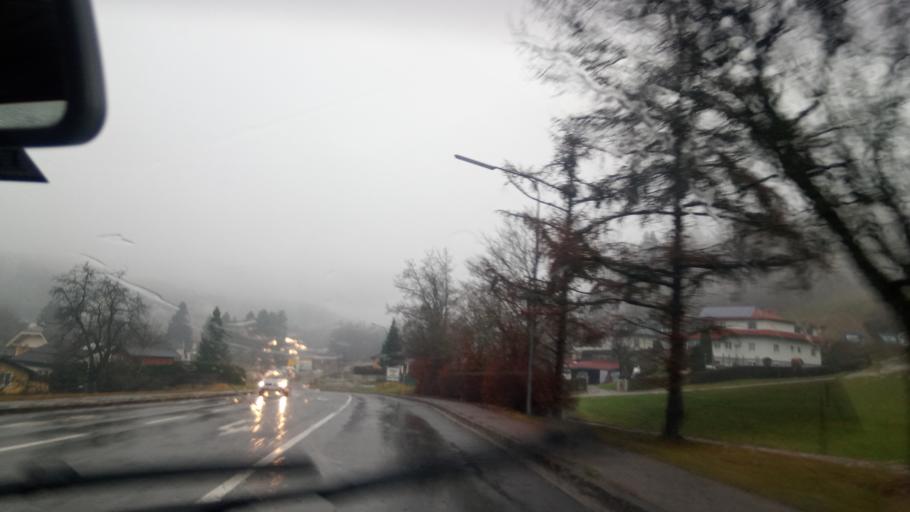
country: AT
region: Carinthia
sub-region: Politischer Bezirk Klagenfurt Land
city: Keutschach am See
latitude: 46.5909
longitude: 14.1726
